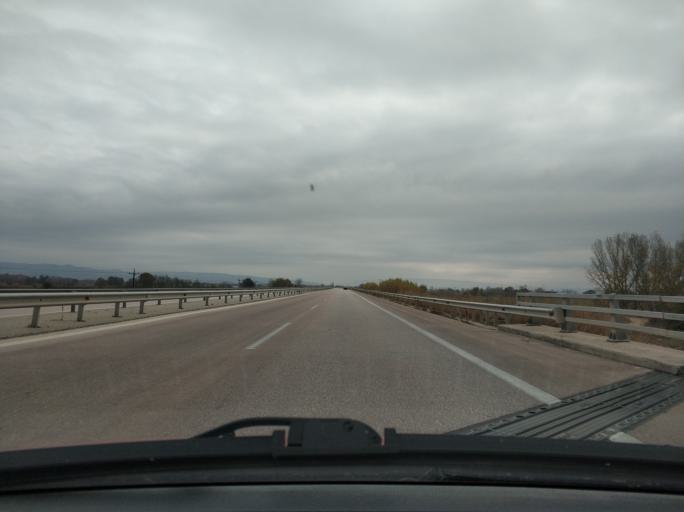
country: GR
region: Central Macedonia
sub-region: Nomos Thessalonikis
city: Lagkadas
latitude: 40.7289
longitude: 23.0640
